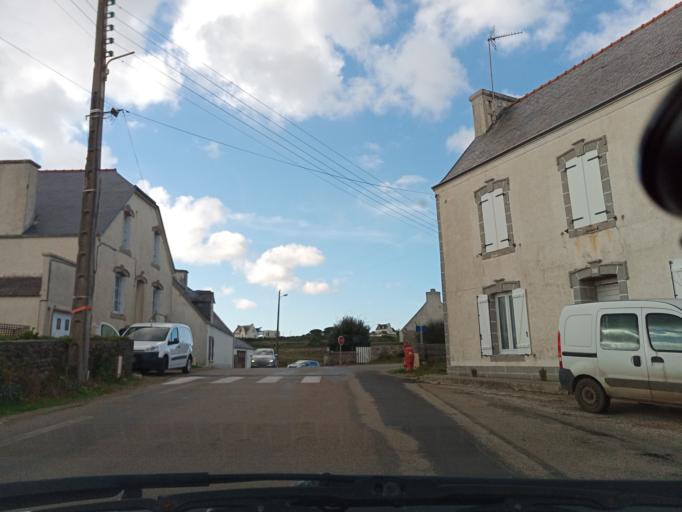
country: FR
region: Brittany
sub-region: Departement du Finistere
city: Plouhinec
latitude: 47.9849
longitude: -4.4614
